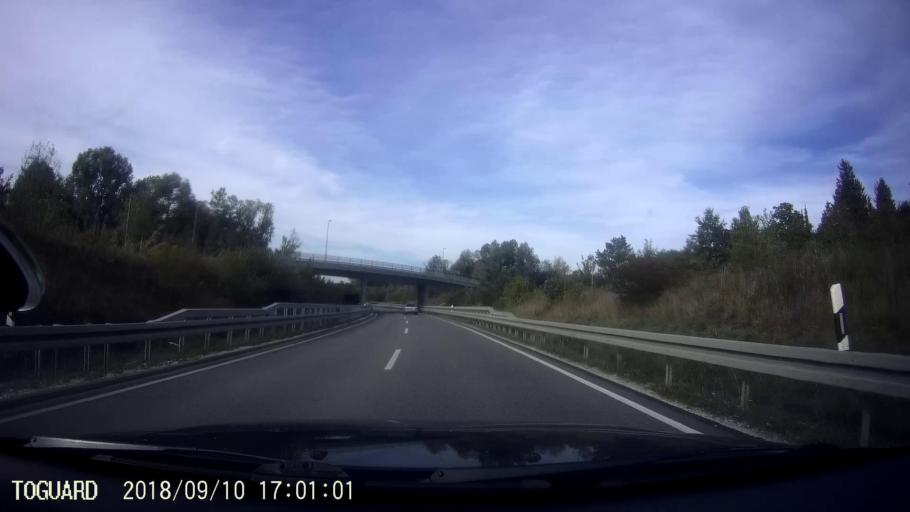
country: CH
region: Thurgau
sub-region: Kreuzlingen District
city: Gottlieben
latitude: 47.6903
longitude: 9.1368
